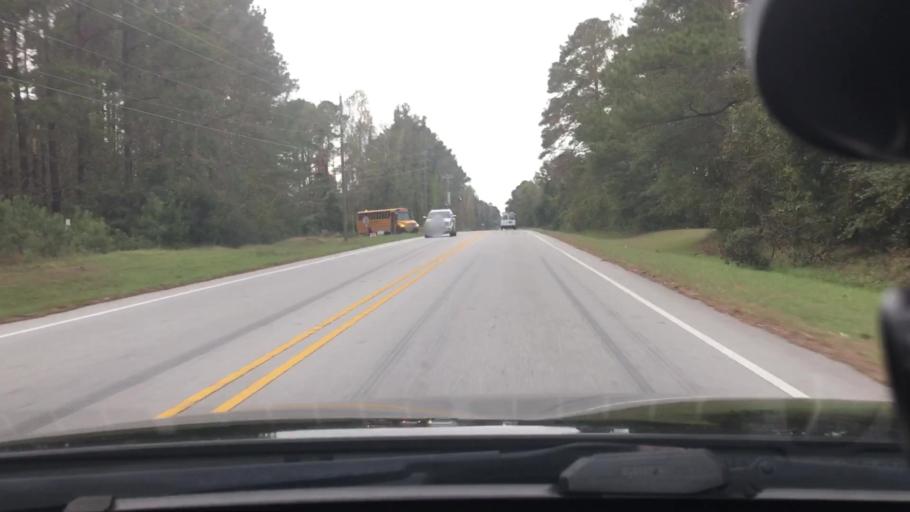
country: US
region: North Carolina
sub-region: Craven County
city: New Bern
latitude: 35.1959
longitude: -77.0546
